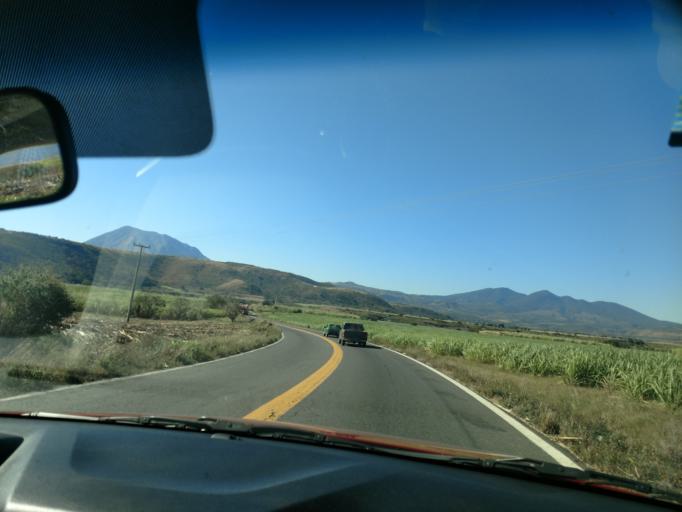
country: MX
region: Nayarit
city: San Pedro Lagunillas
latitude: 21.1499
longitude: -104.6103
